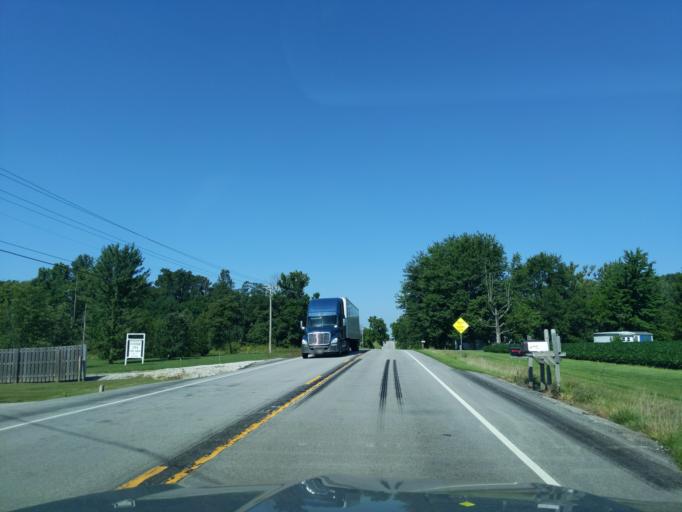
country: US
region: Indiana
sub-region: Ripley County
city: Osgood
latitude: 39.0750
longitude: -85.3272
